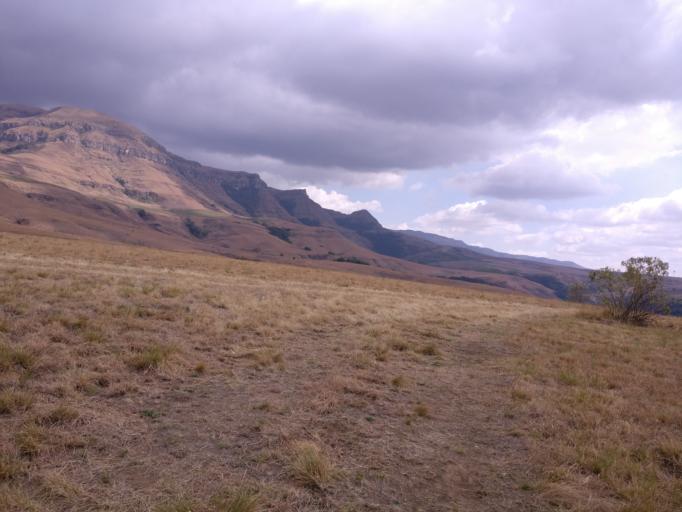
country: ZA
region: KwaZulu-Natal
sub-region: uThukela District Municipality
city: Bergville
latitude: -29.0164
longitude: 29.4134
